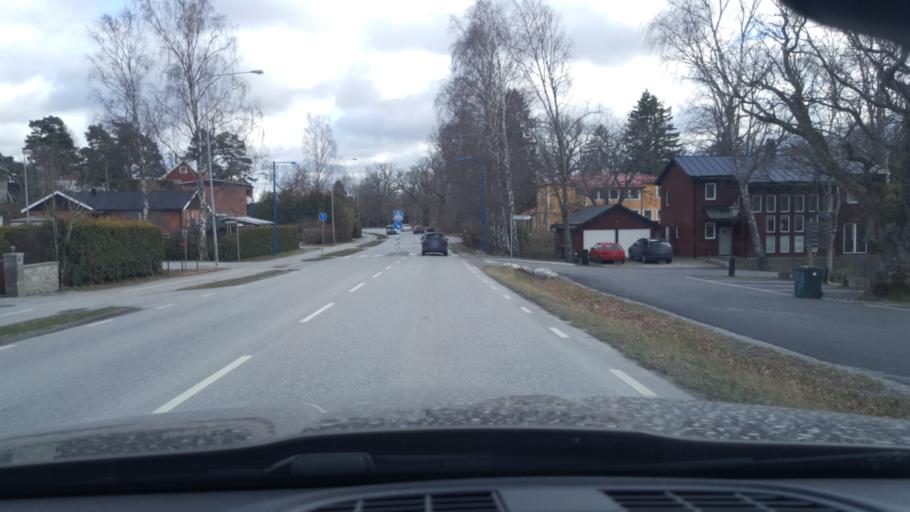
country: SE
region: Stockholm
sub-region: Osterakers Kommun
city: Akersberga
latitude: 59.4909
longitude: 18.2864
